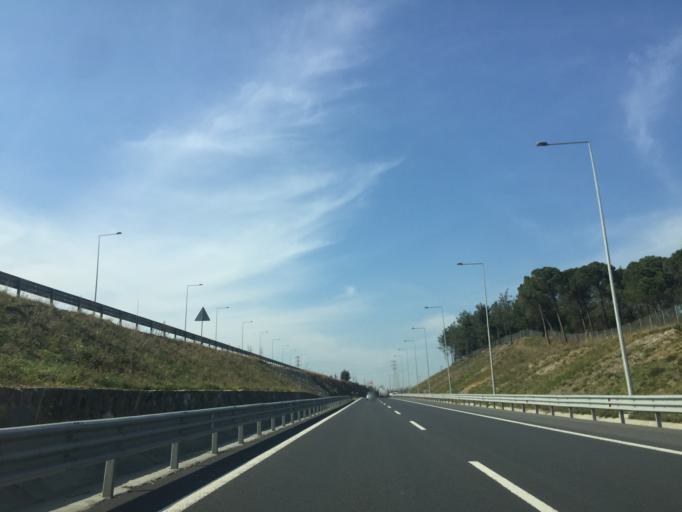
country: TR
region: Istanbul
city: Umraniye
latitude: 41.0520
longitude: 29.1233
